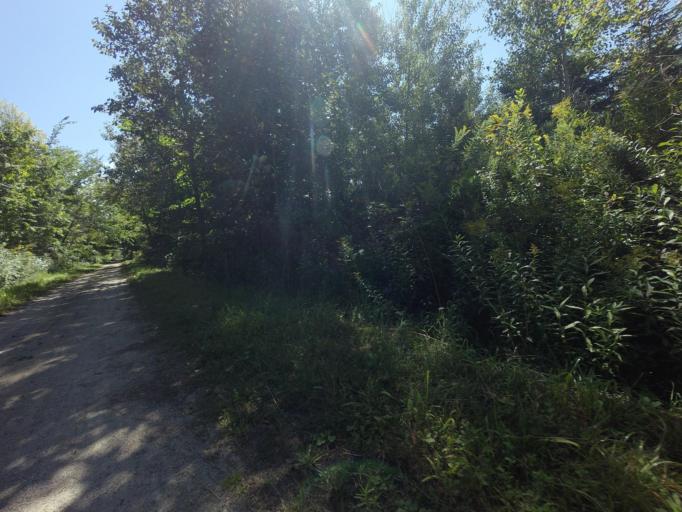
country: CA
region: Ontario
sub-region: Wellington County
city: Guelph
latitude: 43.7396
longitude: -80.3559
